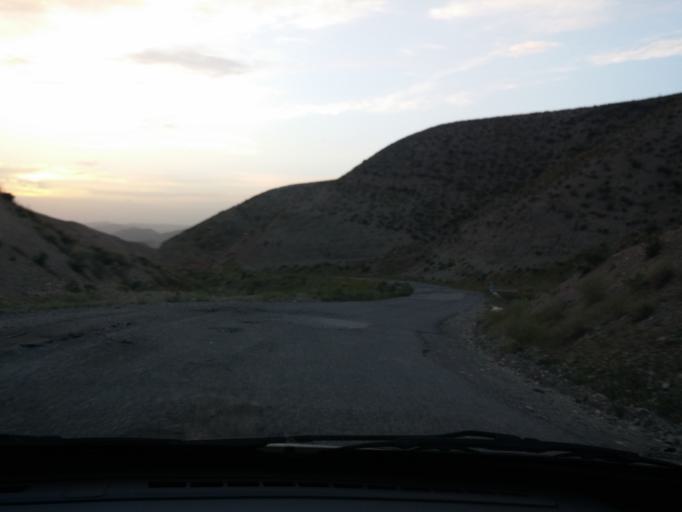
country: IR
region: Semnan
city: Istgah-e Rah Ahan-e Garmsar
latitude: 35.5280
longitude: 52.3205
